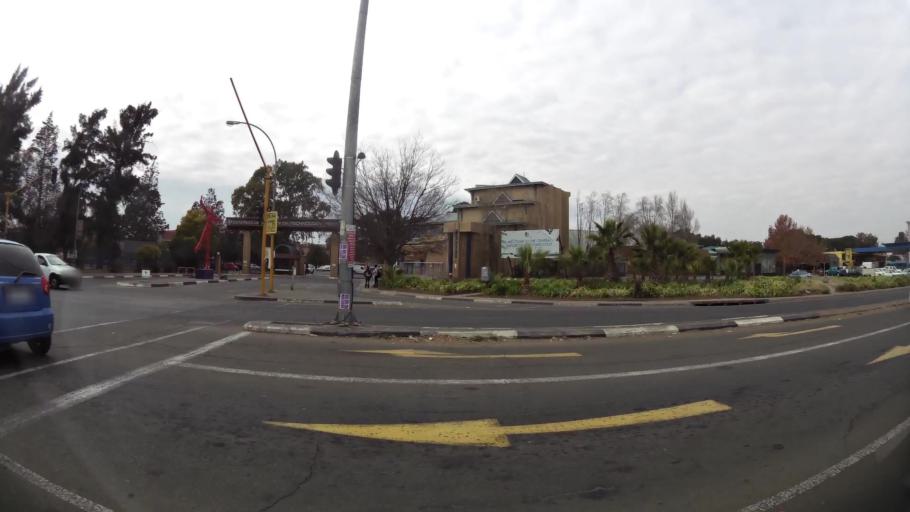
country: ZA
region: Orange Free State
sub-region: Mangaung Metropolitan Municipality
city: Bloemfontein
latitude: -29.1214
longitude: 26.2121
